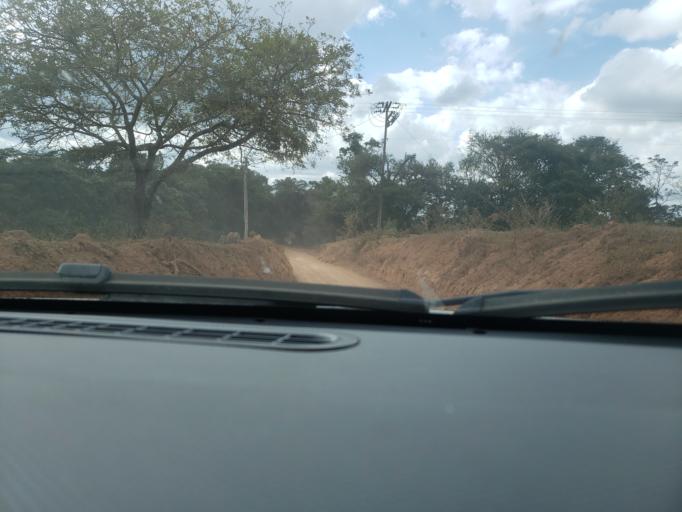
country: BR
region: Minas Gerais
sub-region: Campo Belo
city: Campo Belo
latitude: -20.9187
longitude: -45.2948
